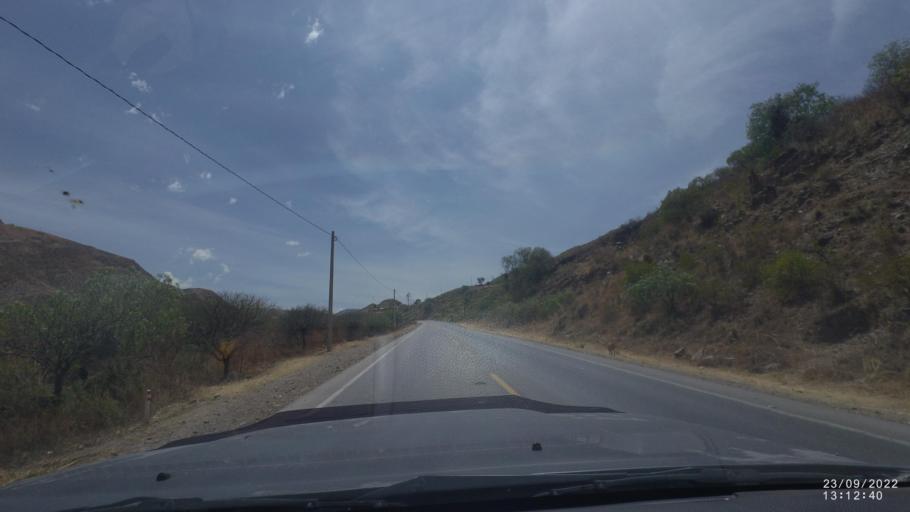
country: BO
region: Cochabamba
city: Irpa Irpa
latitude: -17.6337
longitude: -66.3721
